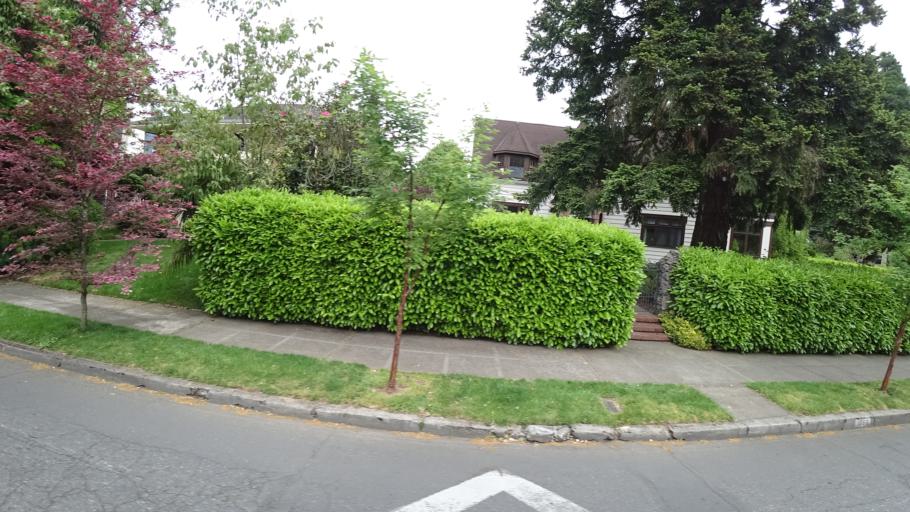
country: US
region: Oregon
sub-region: Multnomah County
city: Lents
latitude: 45.5152
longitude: -122.6068
